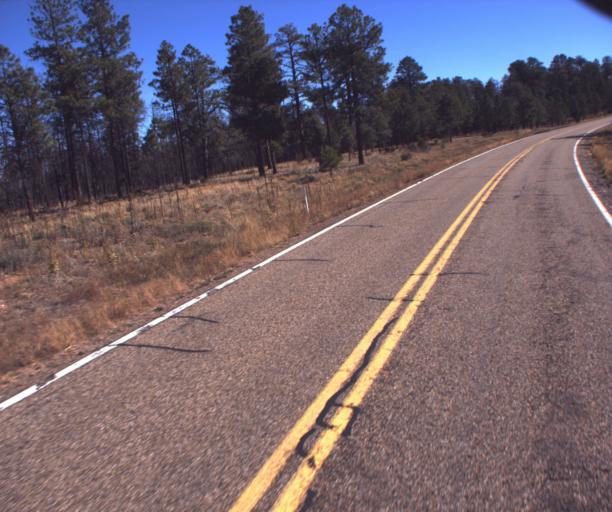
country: US
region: Arizona
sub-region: Coconino County
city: Fredonia
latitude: 36.7435
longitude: -112.2346
